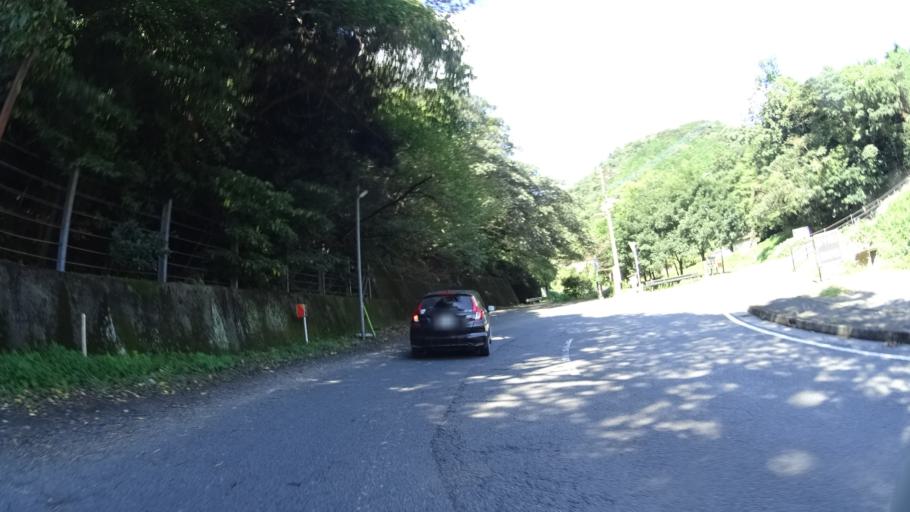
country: JP
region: Oita
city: Beppu
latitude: 33.3167
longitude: 131.4529
